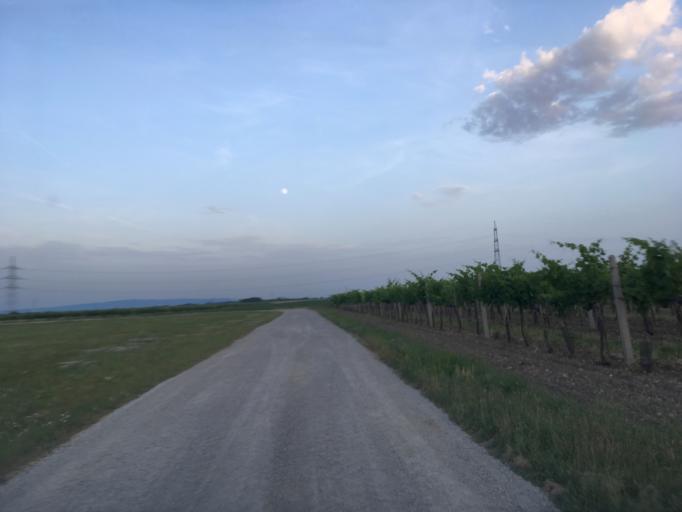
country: AT
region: Lower Austria
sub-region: Politischer Bezirk Baden
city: Tattendorf
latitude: 47.9449
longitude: 16.2947
